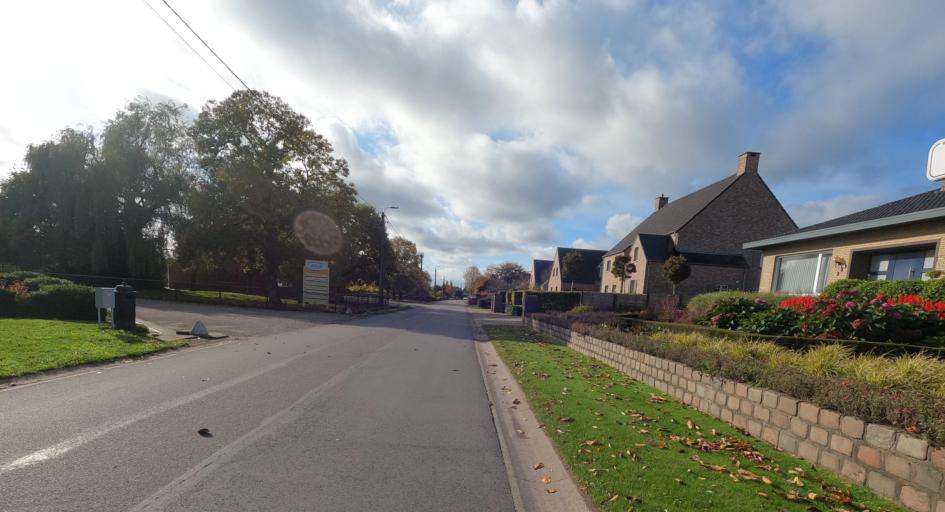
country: BE
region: Flanders
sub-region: Provincie Antwerpen
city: Wuustwezel
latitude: 51.3817
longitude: 4.5656
